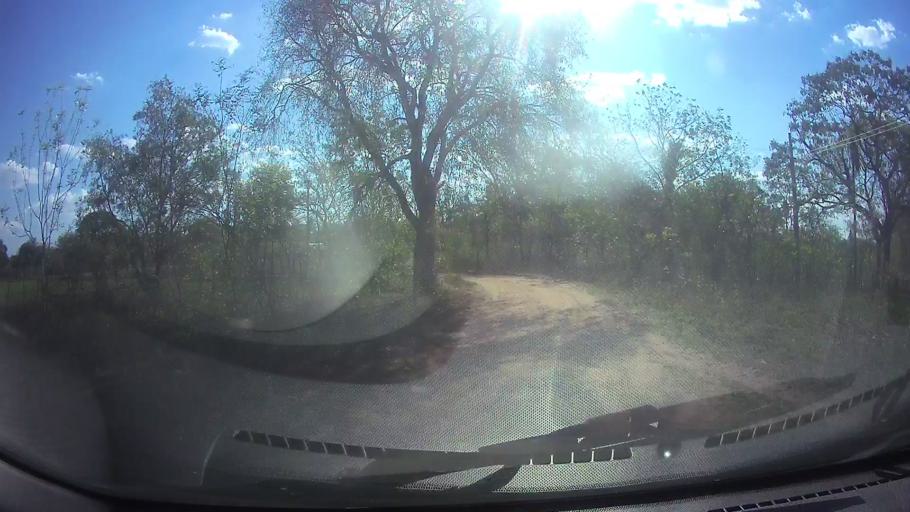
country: PY
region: Cordillera
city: Arroyos y Esteros
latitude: -24.9777
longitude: -57.1952
